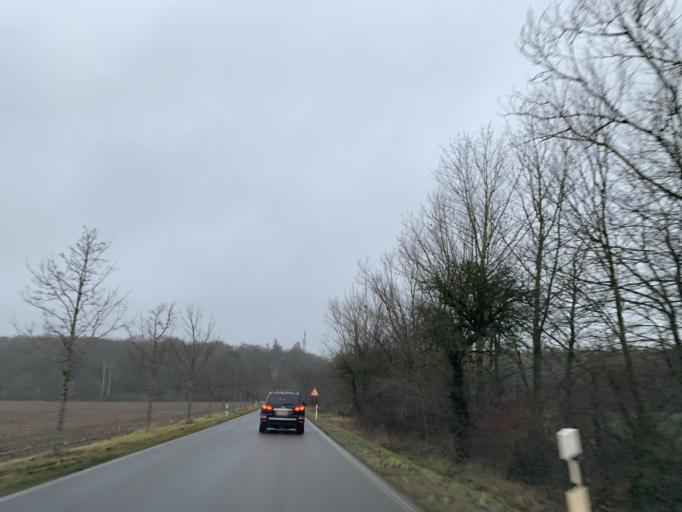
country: DE
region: Mecklenburg-Vorpommern
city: Burg Stargard
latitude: 53.4950
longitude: 13.2655
